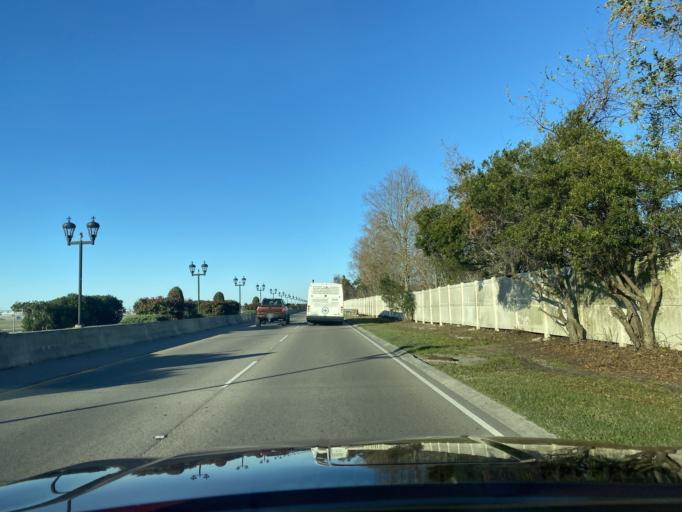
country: US
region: Louisiana
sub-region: Jefferson Parish
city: Kenner
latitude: 29.9947
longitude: -90.2465
